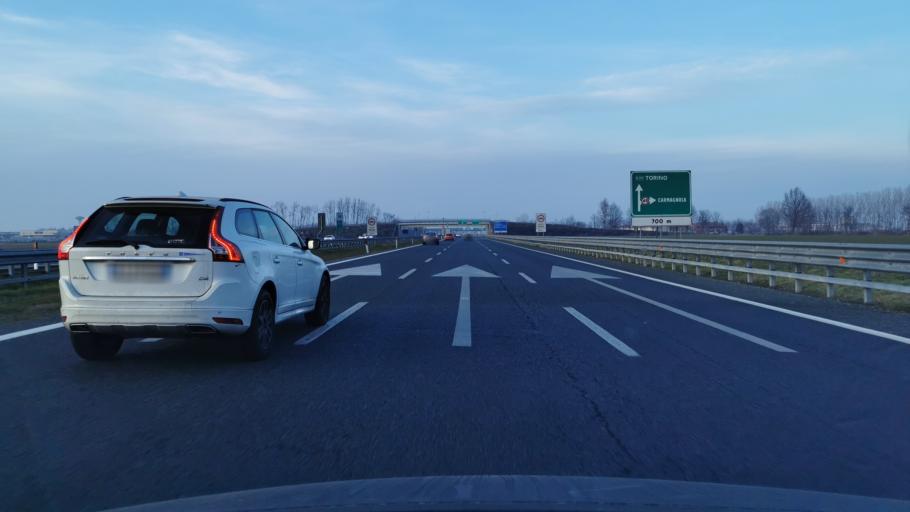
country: IT
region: Piedmont
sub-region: Provincia di Torino
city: Carmagnola
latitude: 44.8444
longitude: 7.7495
